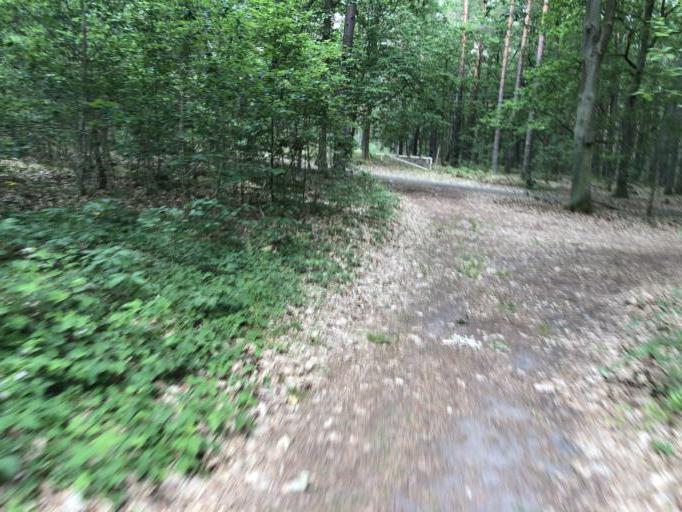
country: DE
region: Brandenburg
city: Gross Koris
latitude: 52.2165
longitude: 13.7042
